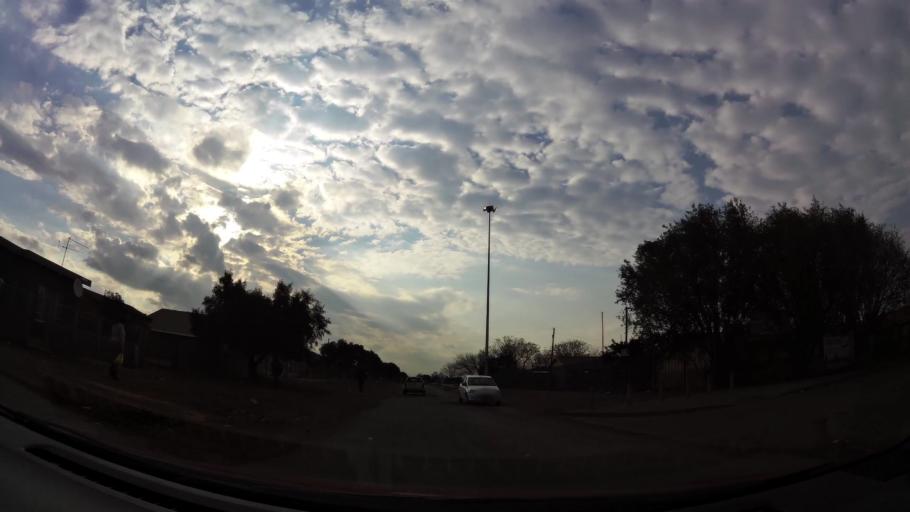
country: ZA
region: Gauteng
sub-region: Sedibeng District Municipality
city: Vanderbijlpark
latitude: -26.6832
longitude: 27.8778
